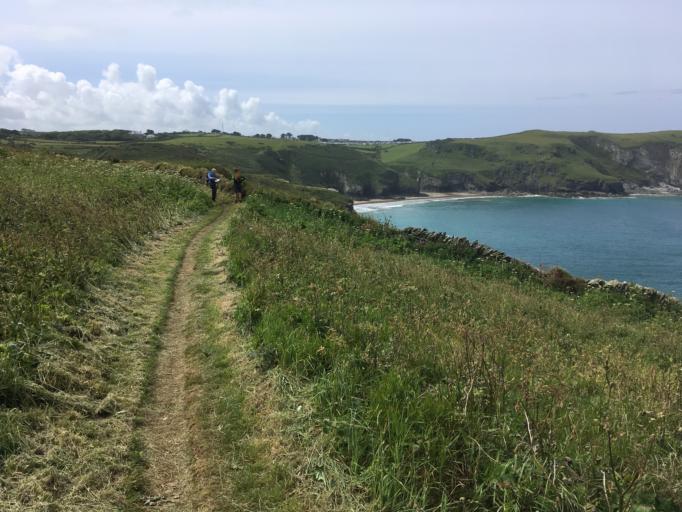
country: GB
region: England
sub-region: Cornwall
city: Tintagel
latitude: 50.6770
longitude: -4.7277
